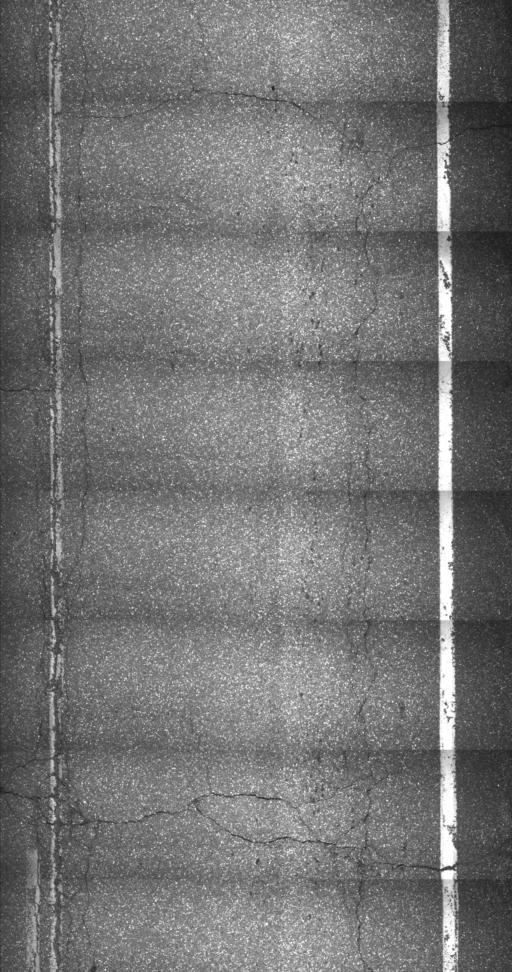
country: US
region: Vermont
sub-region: Orleans County
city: Newport
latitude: 44.8522
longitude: -72.0541
